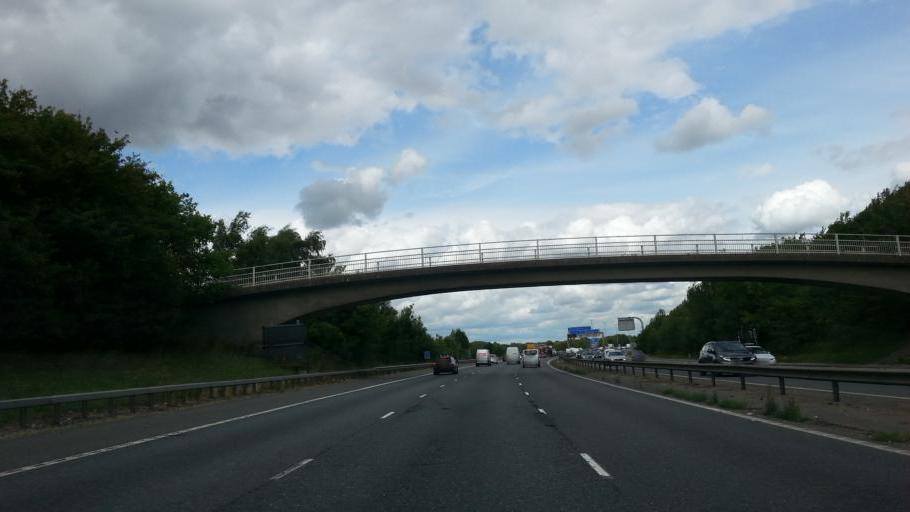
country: GB
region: England
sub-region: Essex
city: Little Hallingbury
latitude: 51.8522
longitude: 0.1845
